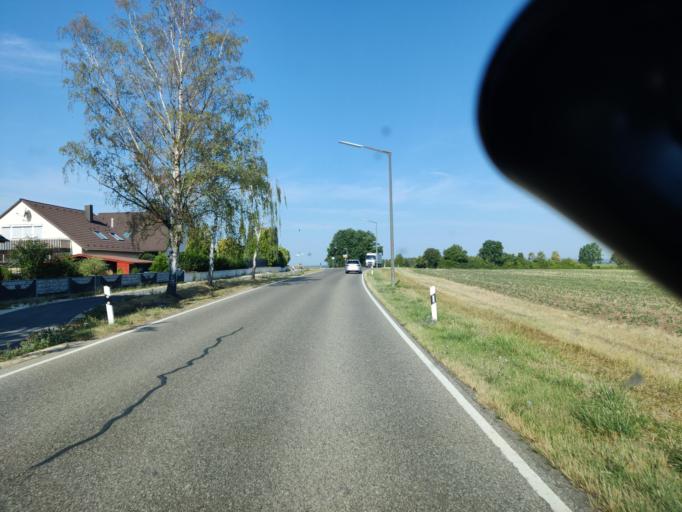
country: DE
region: Bavaria
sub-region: Regierungsbezirk Mittelfranken
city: Hilpoltstein
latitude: 49.1851
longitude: 11.2092
